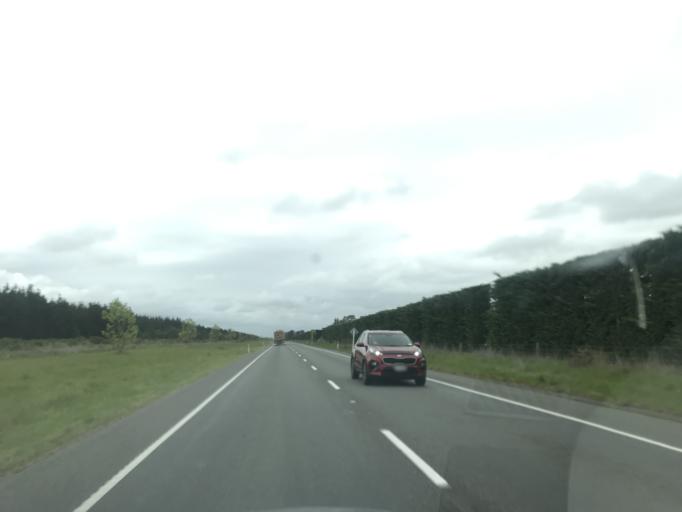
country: NZ
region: Canterbury
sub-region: Ashburton District
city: Tinwald
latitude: -43.9771
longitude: 171.6151
